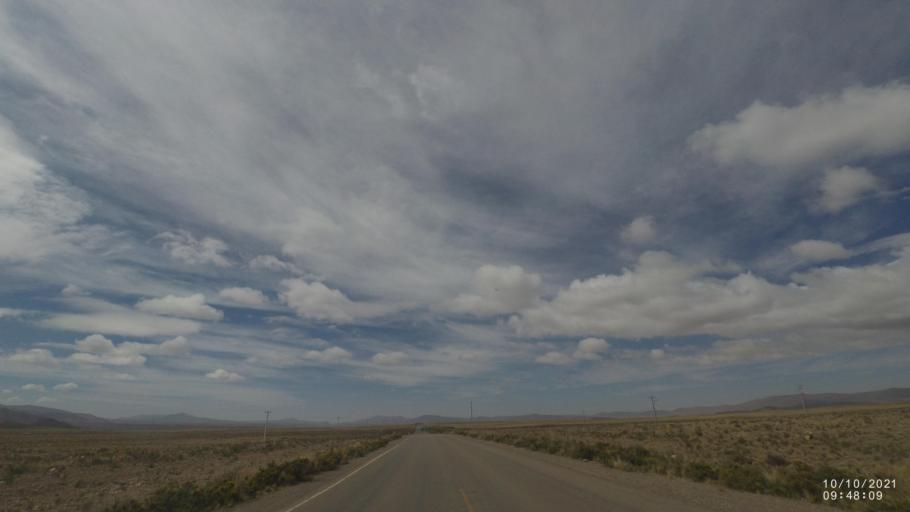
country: BO
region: La Paz
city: Quime
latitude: -17.2050
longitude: -67.3422
